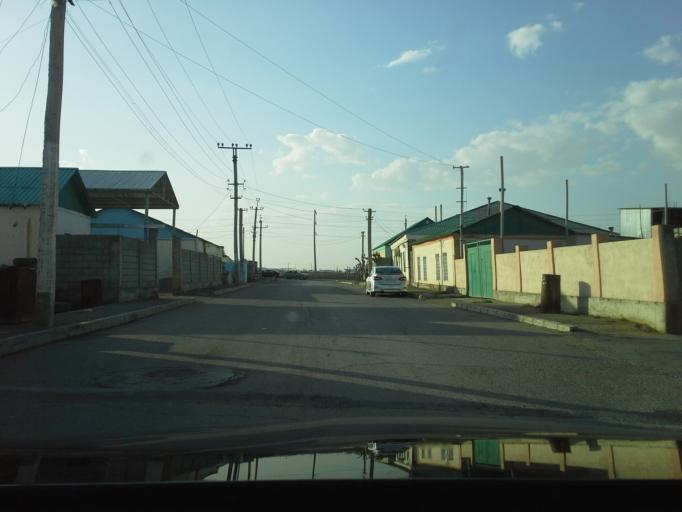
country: TM
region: Ahal
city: Abadan
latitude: 38.0272
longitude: 58.2238
